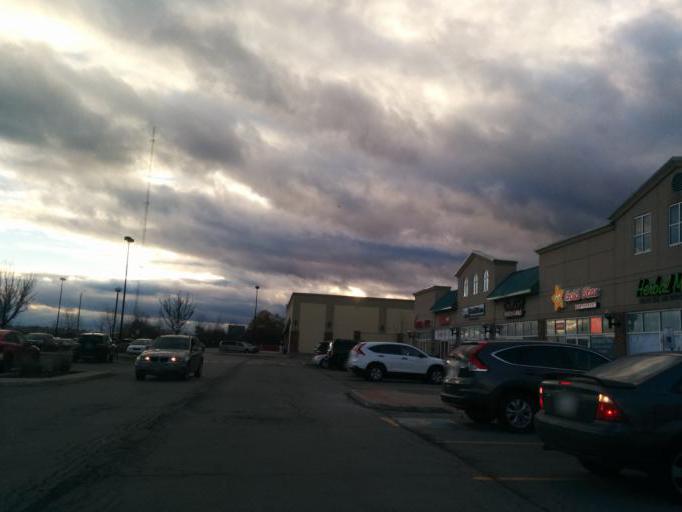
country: CA
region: Ontario
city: Mississauga
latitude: 43.5087
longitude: -79.6315
